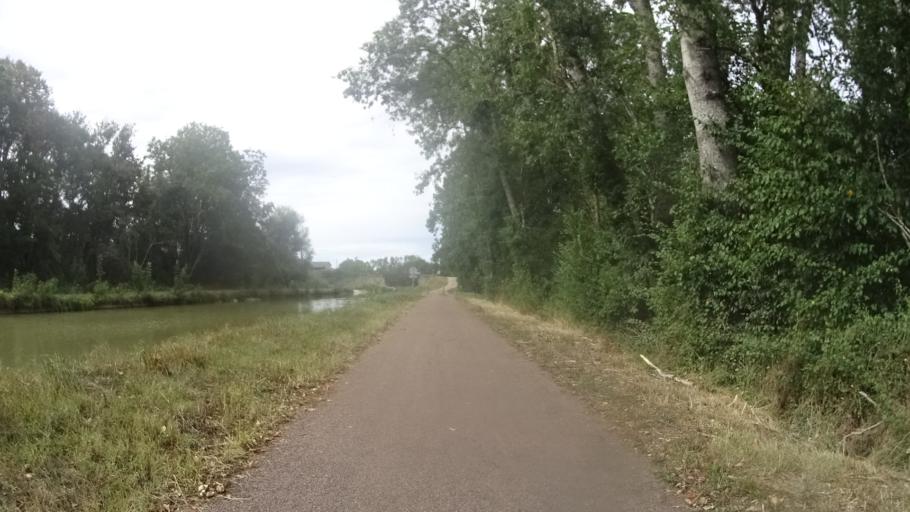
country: FR
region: Bourgogne
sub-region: Departement de la Nievre
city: Sermoise-sur-Loire
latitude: 46.9579
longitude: 3.1986
